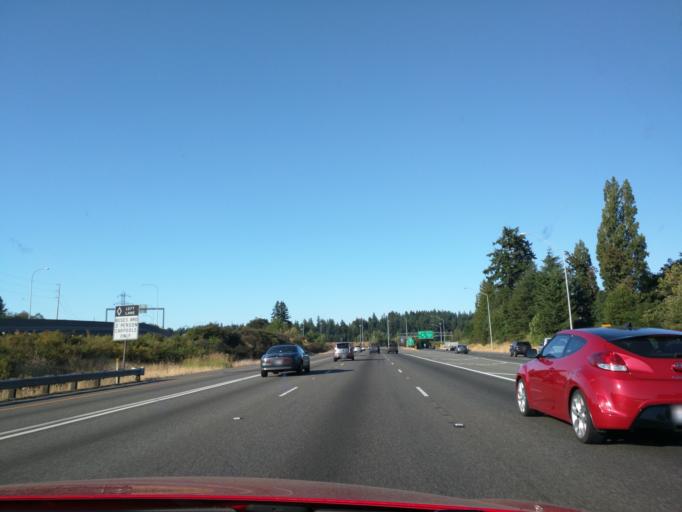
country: US
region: Washington
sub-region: Snohomish County
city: Alderwood Manor
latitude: 47.8267
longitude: -122.2680
